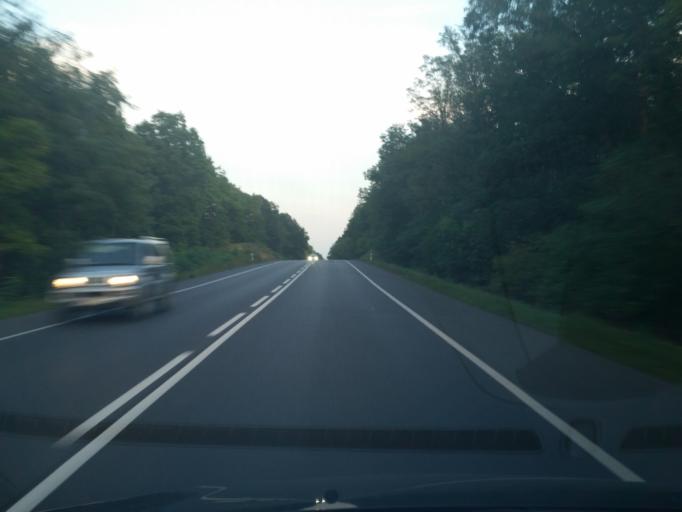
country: PL
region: Masovian Voivodeship
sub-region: Powiat warszawski zachodni
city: Kielpin
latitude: 52.3913
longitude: 20.8757
